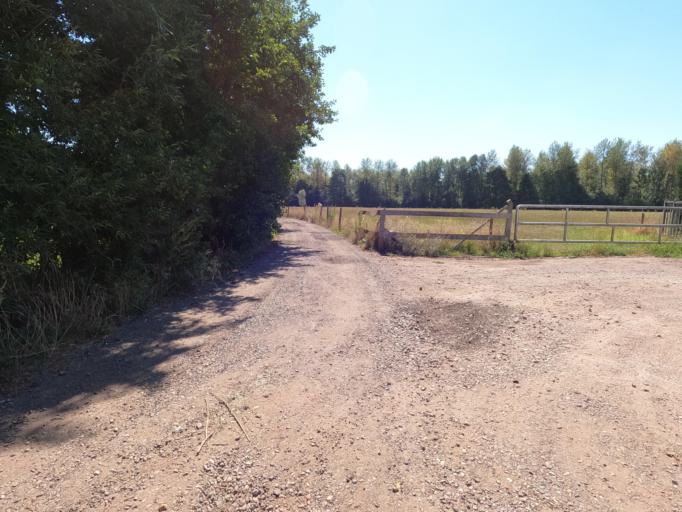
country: BE
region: Flanders
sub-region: Provincie Antwerpen
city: Ranst
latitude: 51.2085
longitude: 4.5714
